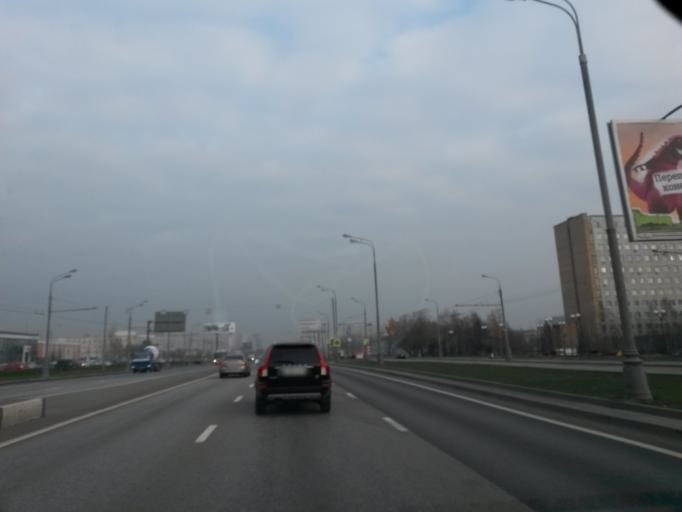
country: RU
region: Moscow
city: Chertanovo Yuzhnoye
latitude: 55.6121
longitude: 37.6101
